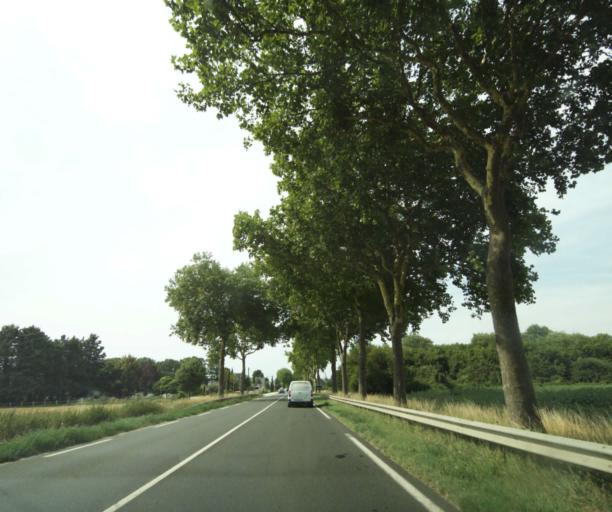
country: FR
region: Centre
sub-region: Departement d'Indre-et-Loire
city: Charentilly
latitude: 47.4629
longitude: 0.6224
